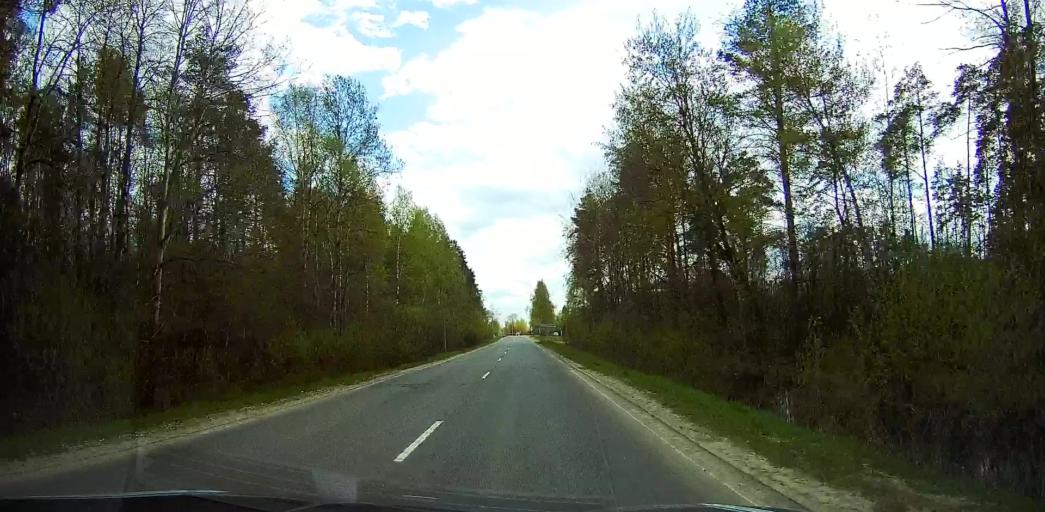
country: RU
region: Moskovskaya
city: Davydovo
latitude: 55.6508
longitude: 38.7550
